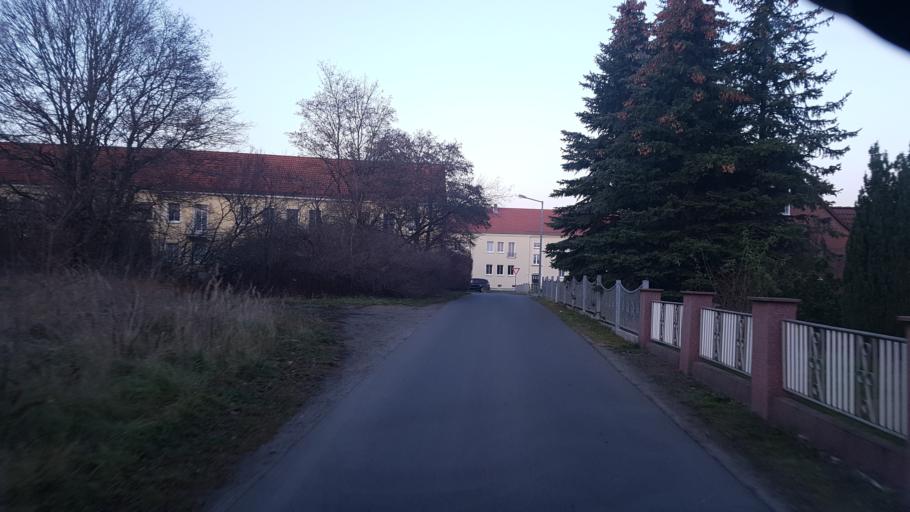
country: DE
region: Brandenburg
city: Lauchhammer
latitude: 51.4935
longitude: 13.7497
